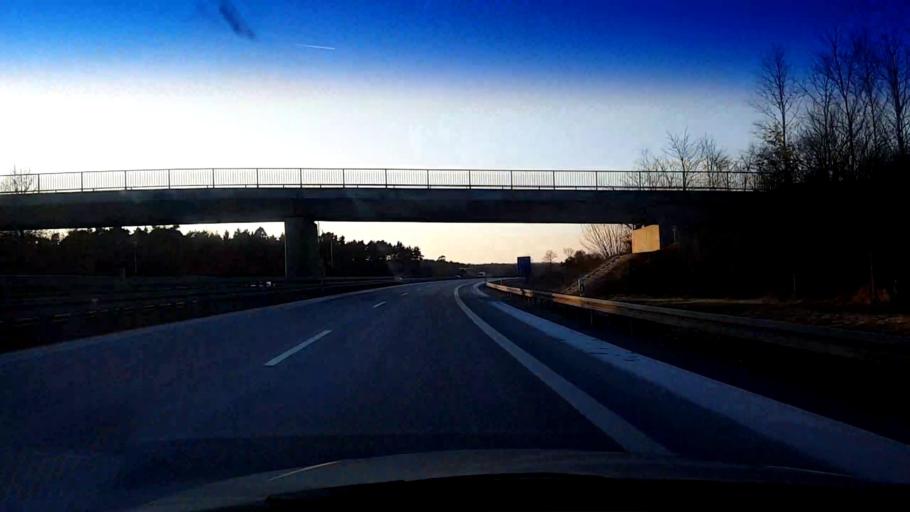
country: DE
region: Bavaria
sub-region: Upper Franconia
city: Kasendorf
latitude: 50.0069
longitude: 11.3330
